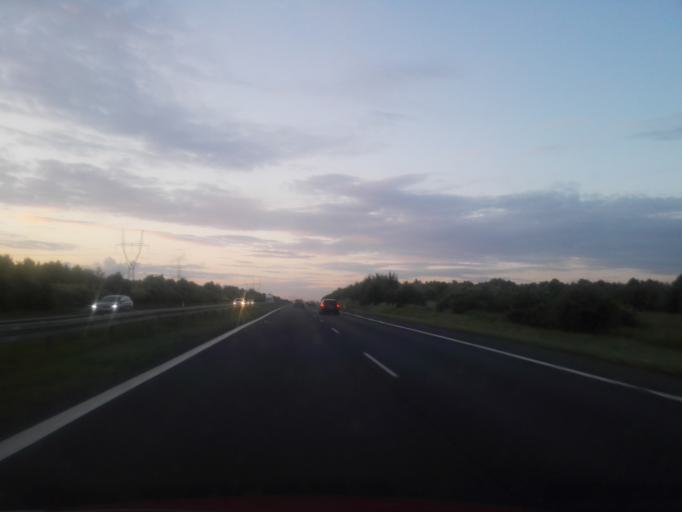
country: PL
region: Lodz Voivodeship
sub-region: Powiat radomszczanski
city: Radomsko
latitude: 51.0868
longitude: 19.3748
